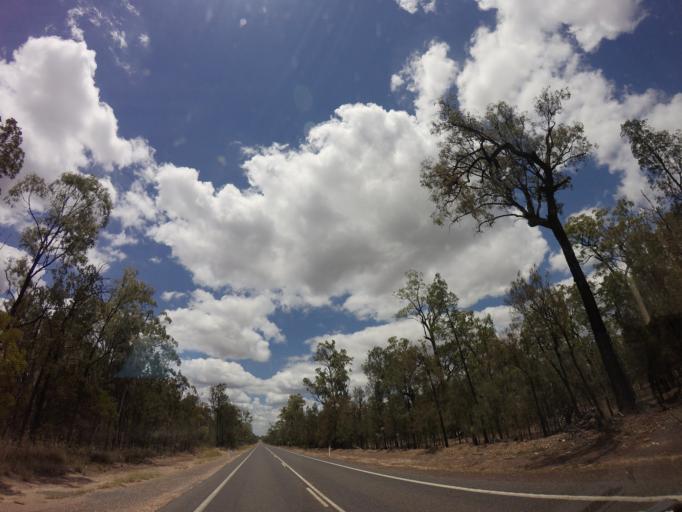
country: AU
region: Queensland
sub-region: Goondiwindi
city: Goondiwindi
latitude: -28.0297
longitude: 150.8334
